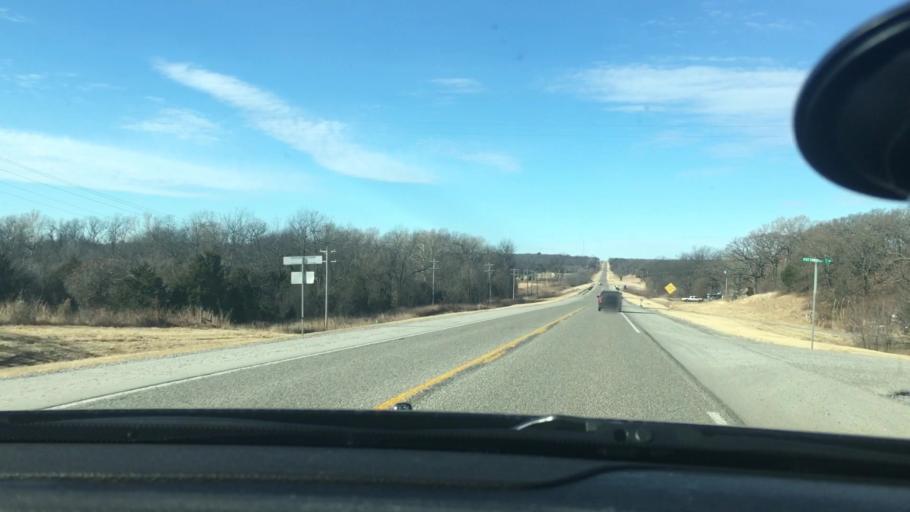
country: US
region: Oklahoma
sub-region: Cleveland County
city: Lexington
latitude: 35.0148
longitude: -97.1418
